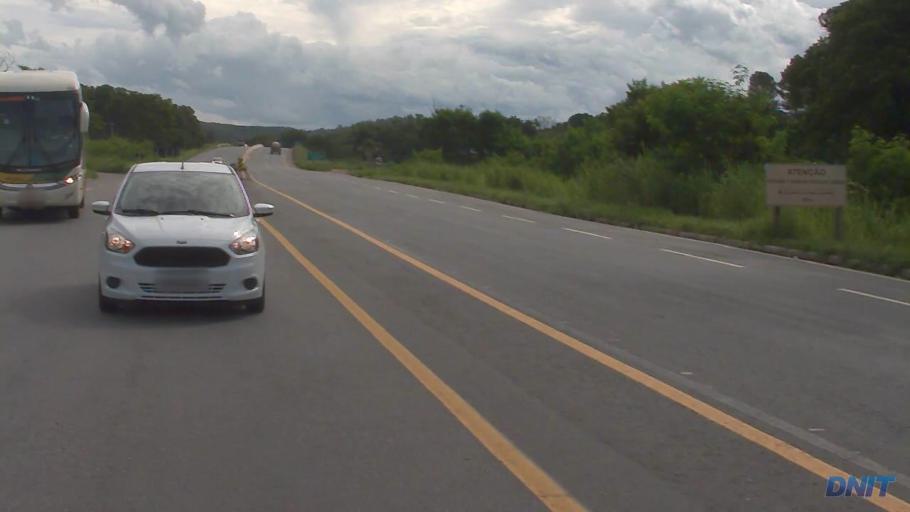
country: BR
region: Minas Gerais
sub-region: Ipaba
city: Ipaba
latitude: -19.3076
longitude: -42.3889
